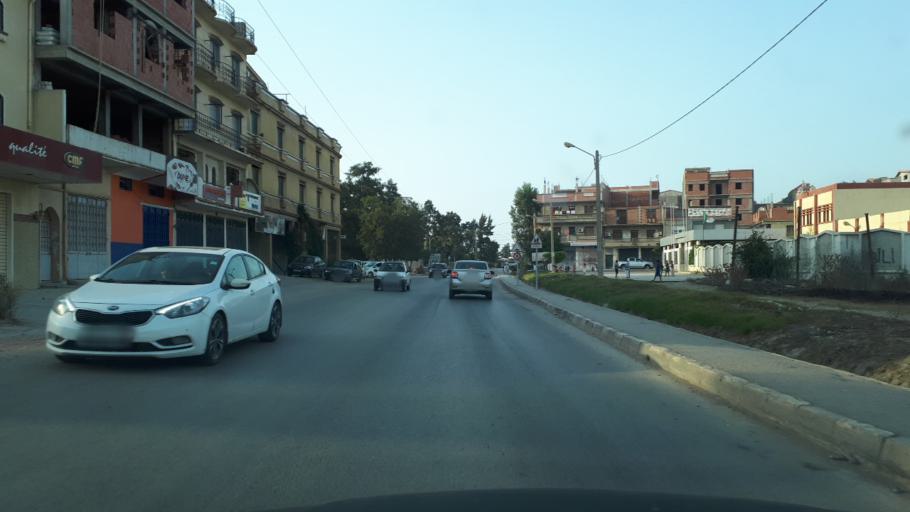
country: DZ
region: Alger
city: Dar el Beida
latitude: 36.7375
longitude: 3.2334
